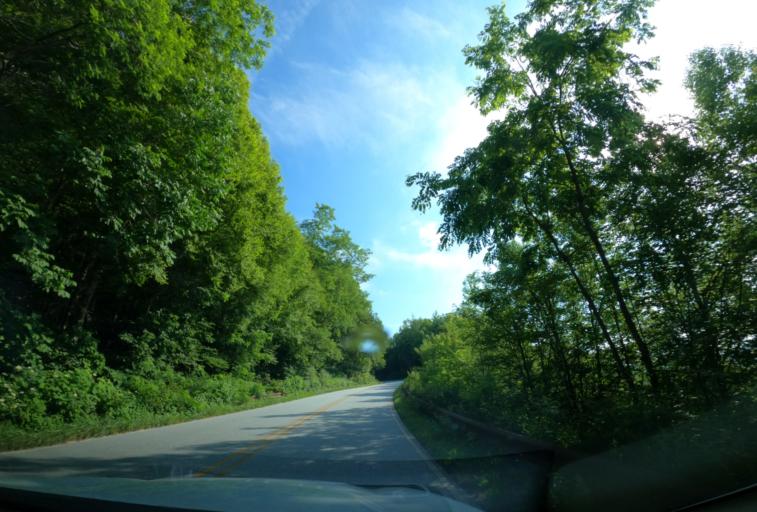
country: US
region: North Carolina
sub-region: Transylvania County
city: Brevard
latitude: 35.2809
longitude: -82.9192
